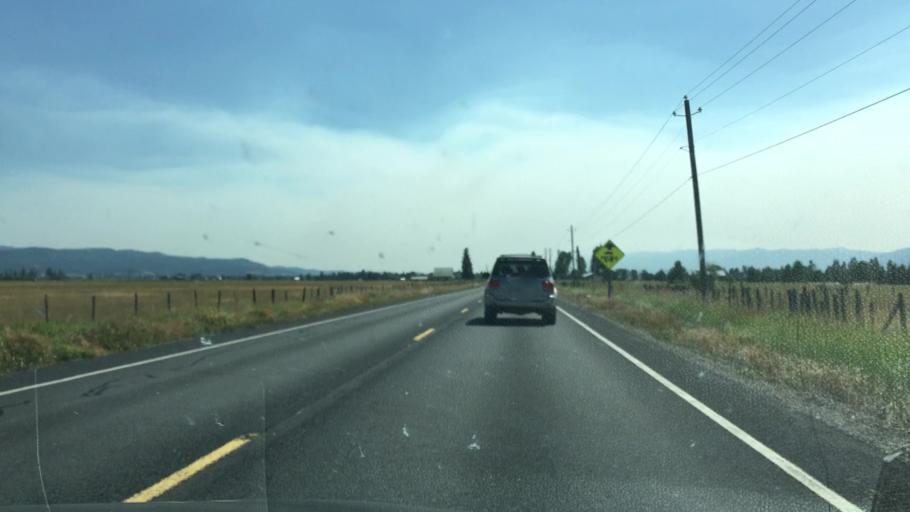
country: US
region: Idaho
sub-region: Valley County
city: McCall
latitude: 44.7516
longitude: -116.0783
